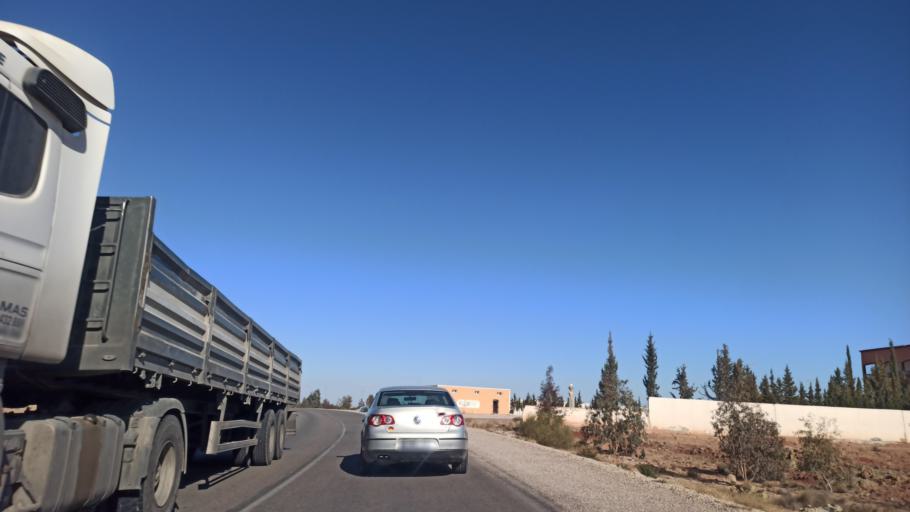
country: TN
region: Sidi Bu Zayd
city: Jilma
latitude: 35.1359
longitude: 9.3598
